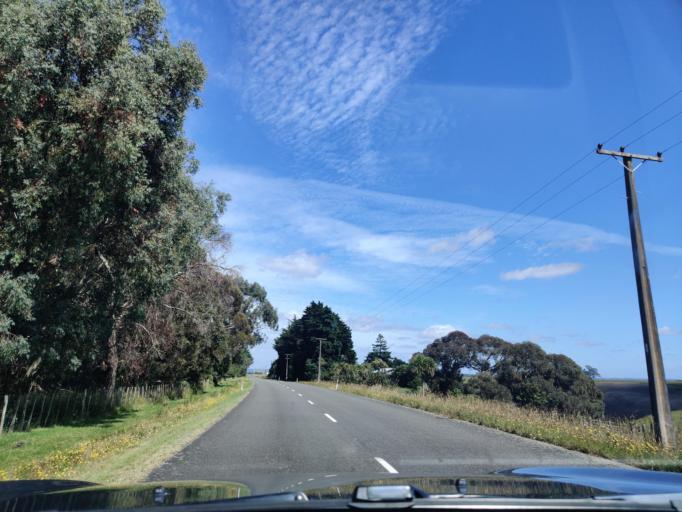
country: NZ
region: Manawatu-Wanganui
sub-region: Rangitikei District
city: Bulls
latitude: -40.1882
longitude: 175.4563
